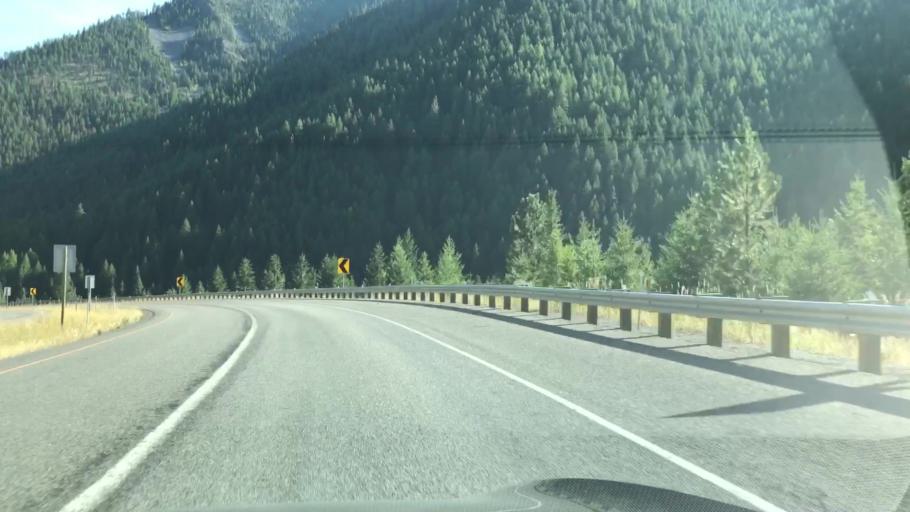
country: US
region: Montana
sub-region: Sanders County
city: Thompson Falls
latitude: 47.3365
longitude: -115.2704
